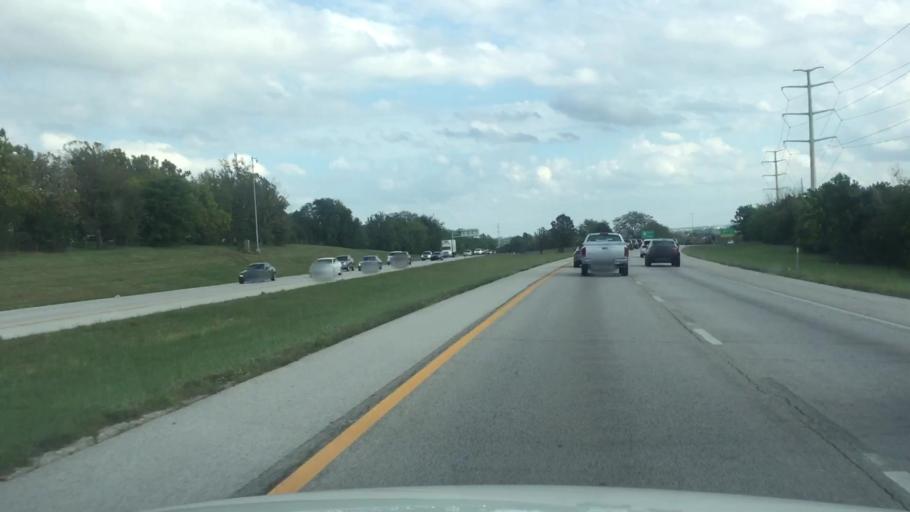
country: US
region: Kansas
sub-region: Johnson County
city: Lenexa
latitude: 38.9047
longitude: -94.6848
